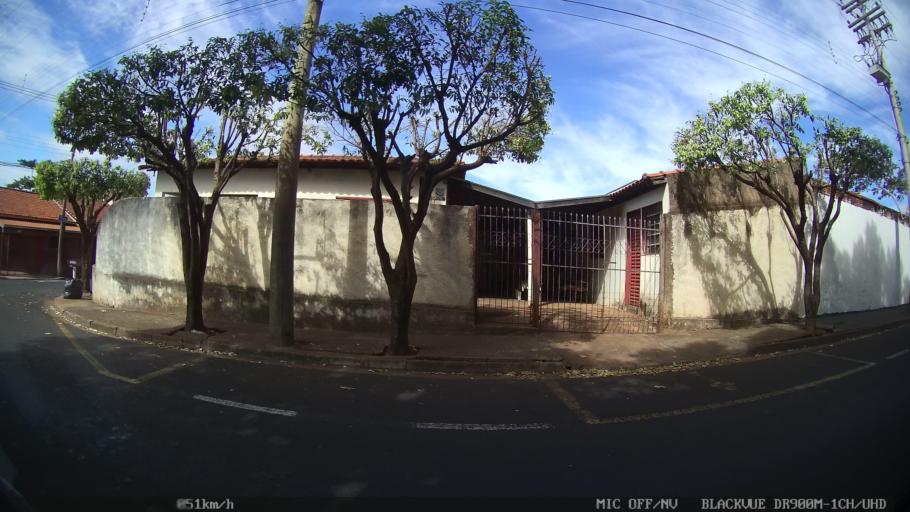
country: BR
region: Sao Paulo
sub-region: Sao Jose Do Rio Preto
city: Sao Jose do Rio Preto
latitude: -20.8320
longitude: -49.3518
